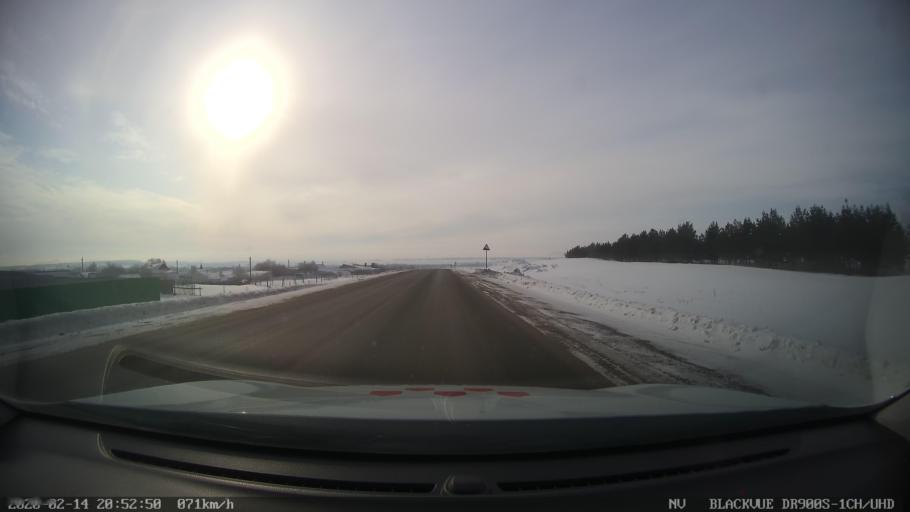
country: RU
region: Tatarstan
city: Kuybyshevskiy Zaton
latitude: 55.2004
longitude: 49.2495
